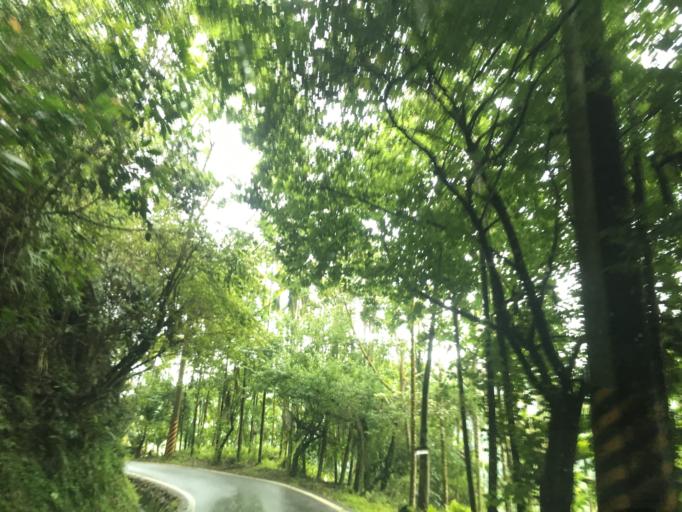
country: TW
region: Taiwan
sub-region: Yunlin
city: Douliu
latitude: 23.5634
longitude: 120.6468
